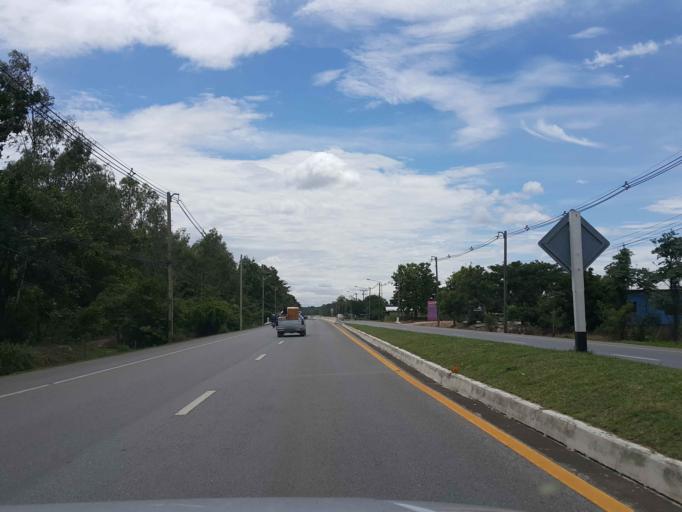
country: TH
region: Sukhothai
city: Ban Dan Lan Hoi
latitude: 17.0020
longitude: 99.5462
